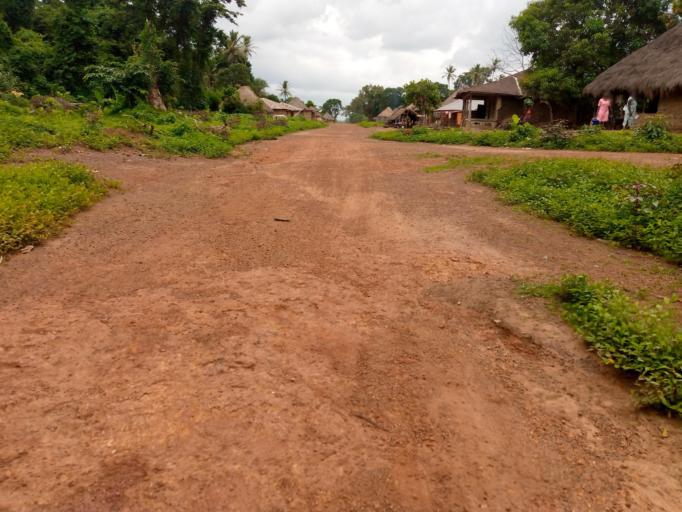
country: SL
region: Southern Province
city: Moyamba
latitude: 8.0886
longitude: -12.4483
